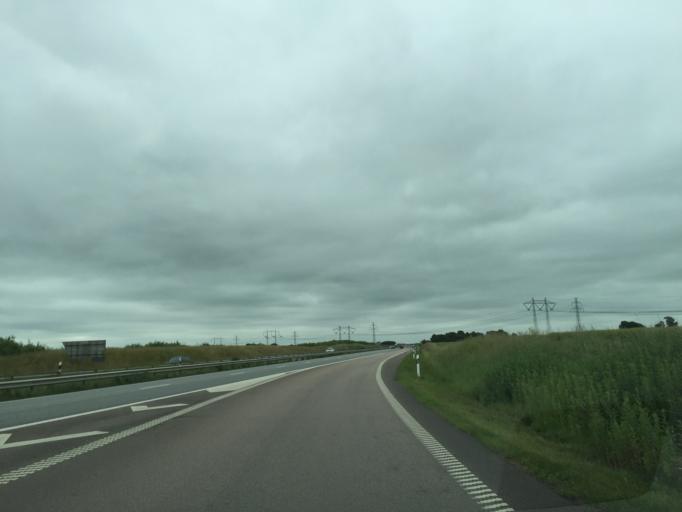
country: SE
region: Skane
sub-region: Kavlinge Kommun
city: Loddekopinge
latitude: 55.7439
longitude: 13.0331
